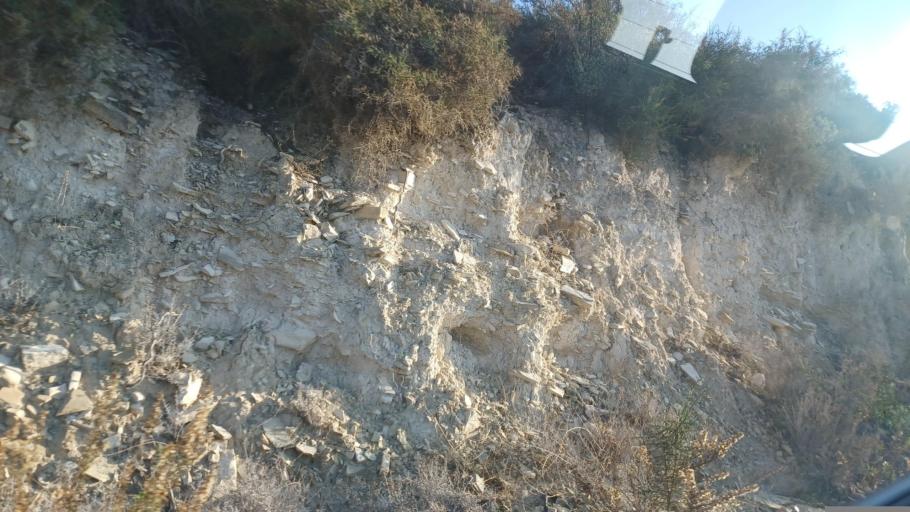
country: CY
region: Larnaka
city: Kofinou
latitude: 34.8280
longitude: 33.3058
